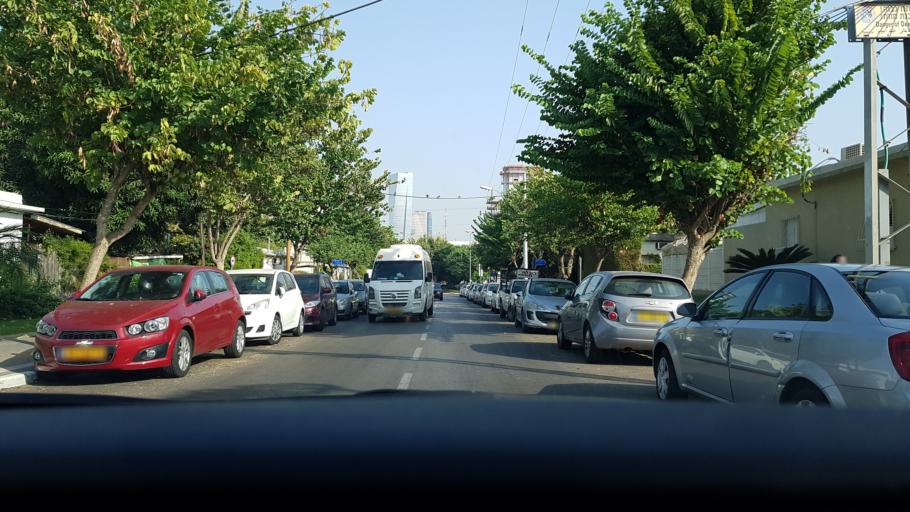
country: IL
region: Tel Aviv
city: Tel Aviv
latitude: 32.0576
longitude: 34.7893
